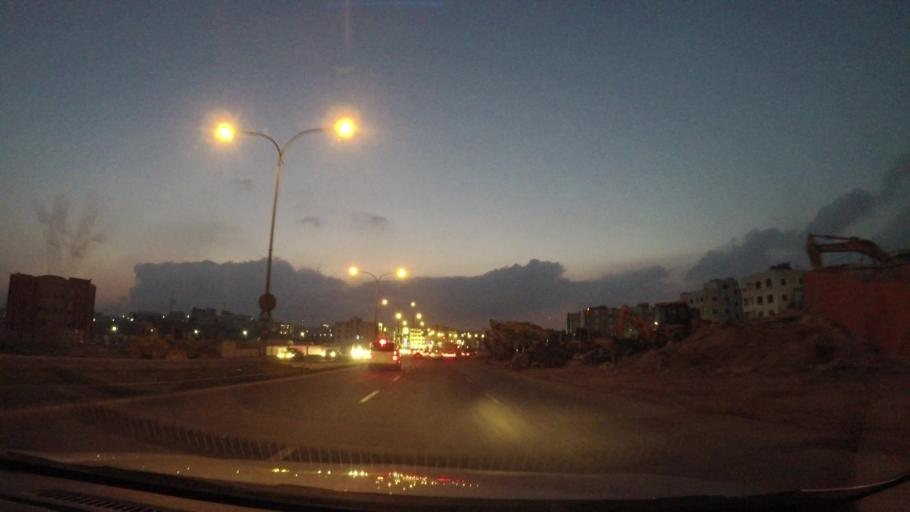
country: JO
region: Amman
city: Al Bunayyat ash Shamaliyah
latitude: 31.8962
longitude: 35.9060
